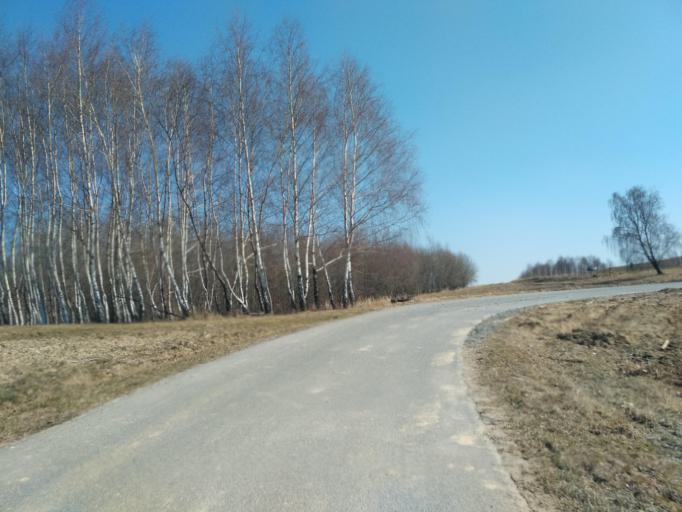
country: PL
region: Subcarpathian Voivodeship
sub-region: Powiat rzeszowski
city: Zglobien
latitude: 49.9824
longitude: 21.8385
